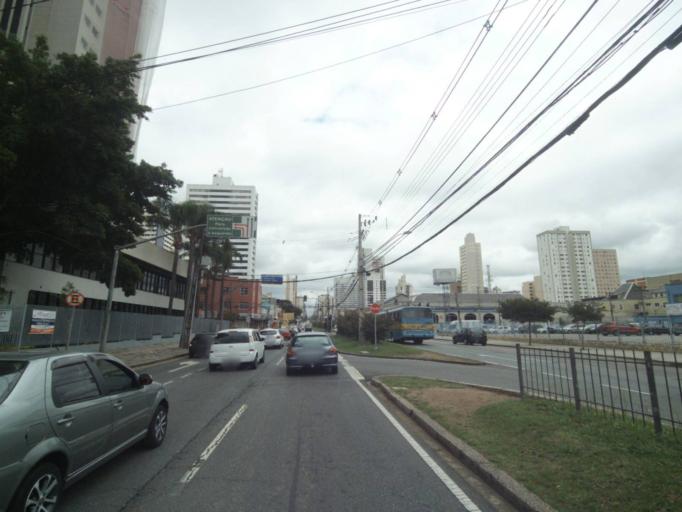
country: BR
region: Parana
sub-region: Curitiba
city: Curitiba
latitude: -25.4348
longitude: -49.2636
